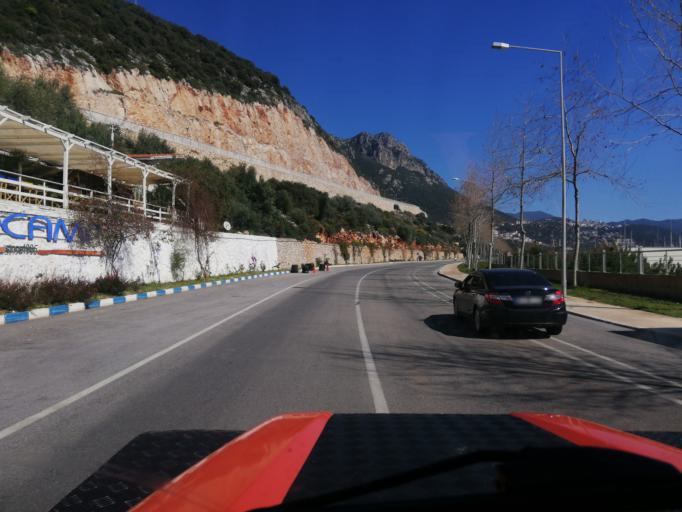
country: TR
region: Antalya
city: Kas
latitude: 36.2071
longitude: 29.6239
